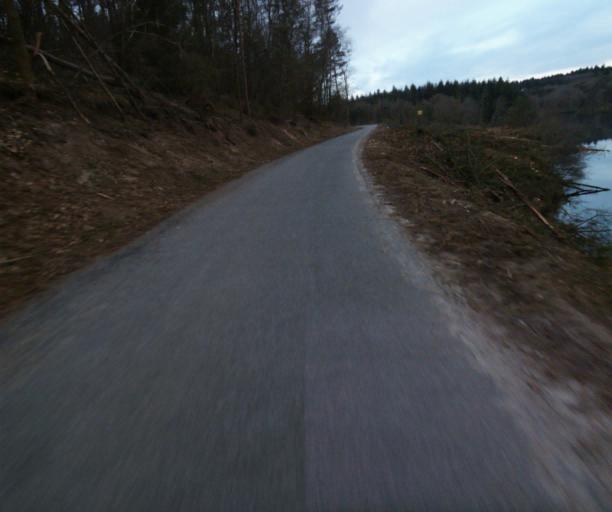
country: FR
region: Limousin
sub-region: Departement de la Correze
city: Correze
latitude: 45.4456
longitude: 1.8393
